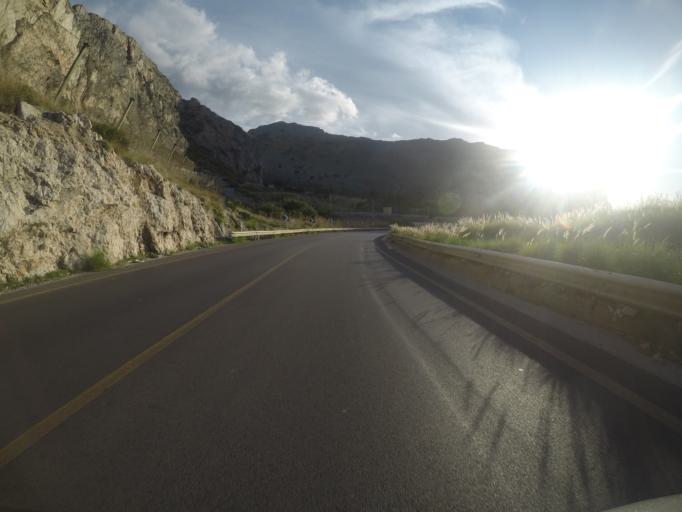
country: IT
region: Sicily
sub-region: Palermo
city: Isola delle Femmine
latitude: 38.2003
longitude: 13.2666
